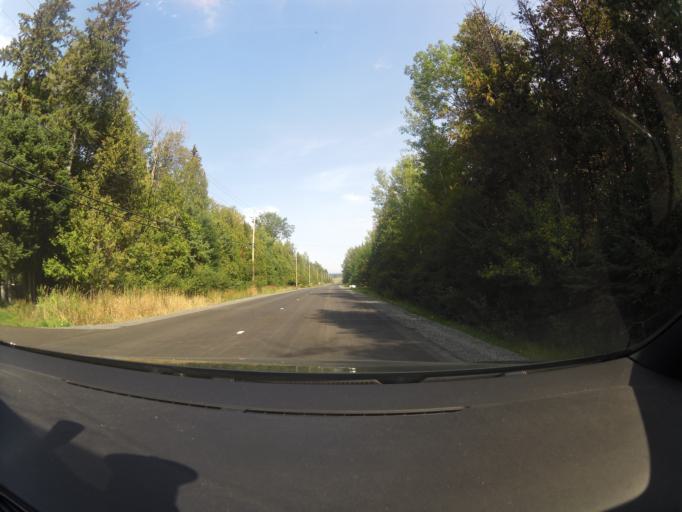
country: CA
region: Ontario
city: Carleton Place
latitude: 45.3435
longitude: -76.1439
